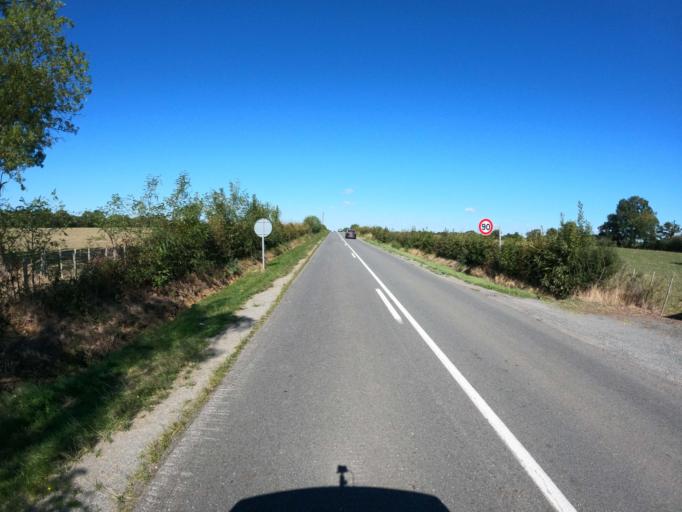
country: FR
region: Poitou-Charentes
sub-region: Departement de la Vienne
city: Lathus-Saint-Remy
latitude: 46.3442
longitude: 0.9516
